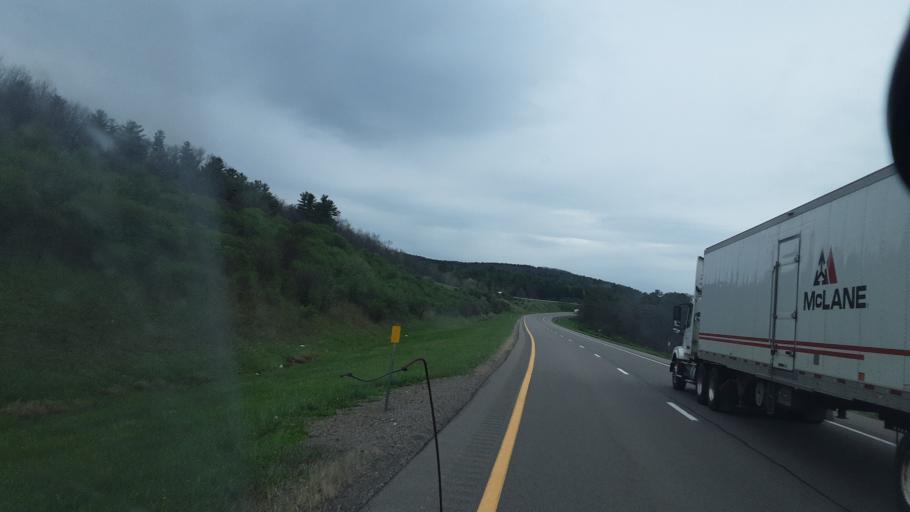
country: US
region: New York
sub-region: Allegany County
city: Belmont
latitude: 42.2978
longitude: -77.9279
